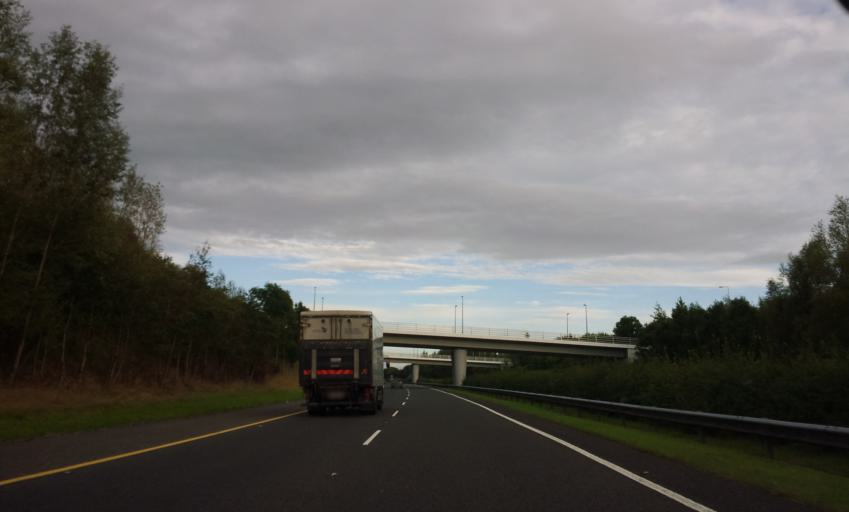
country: IE
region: Munster
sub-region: An Clar
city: Shannon
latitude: 52.7270
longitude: -8.8774
